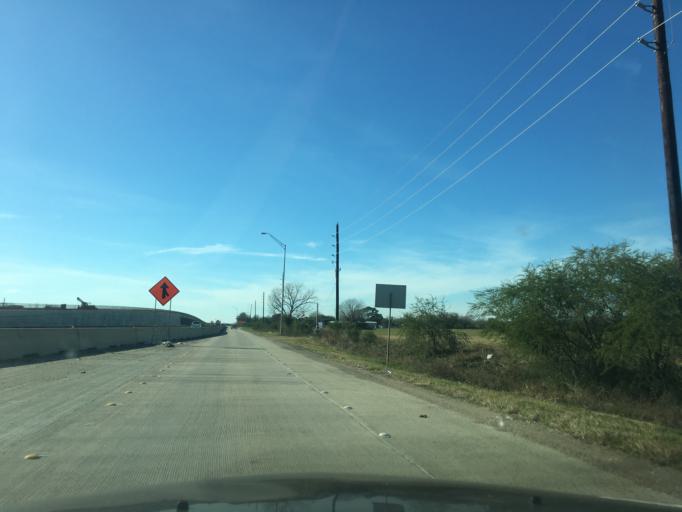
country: US
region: Texas
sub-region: Fort Bend County
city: Rosenberg
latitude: 29.5323
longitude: -95.8152
